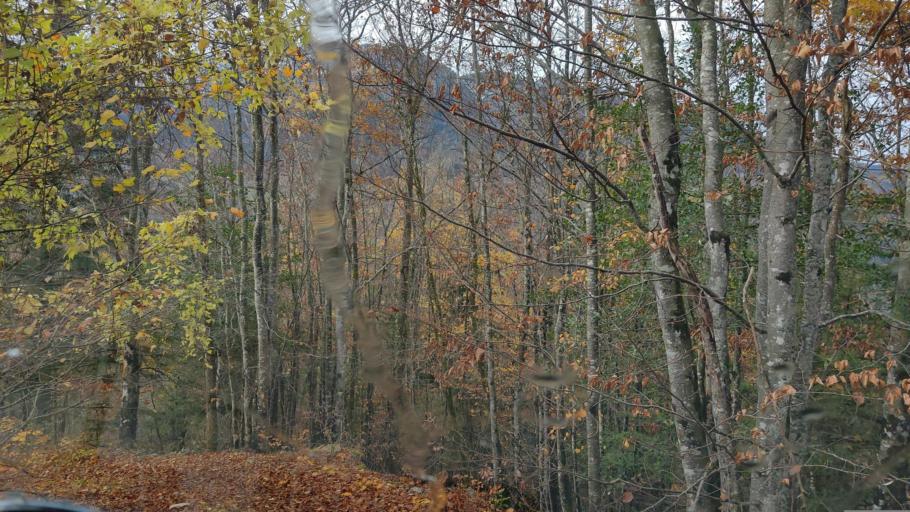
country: FR
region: Rhone-Alpes
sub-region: Departement de l'Isere
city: Saint-Vincent-de-Mercuze
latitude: 45.4167
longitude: 5.8622
